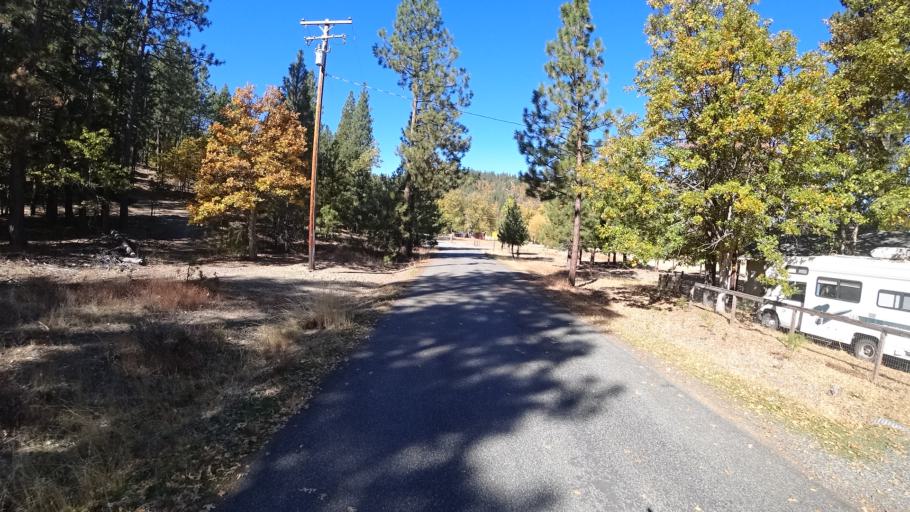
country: US
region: California
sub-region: Siskiyou County
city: Yreka
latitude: 41.5216
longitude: -122.9248
